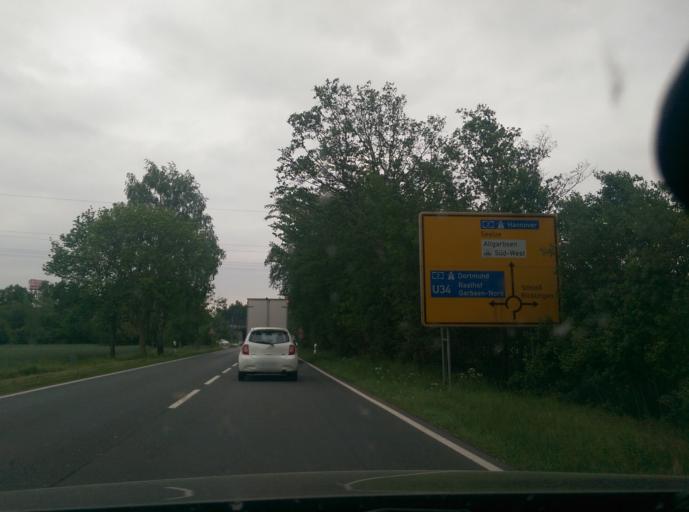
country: DE
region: Lower Saxony
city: Garbsen
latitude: 52.4251
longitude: 9.5728
